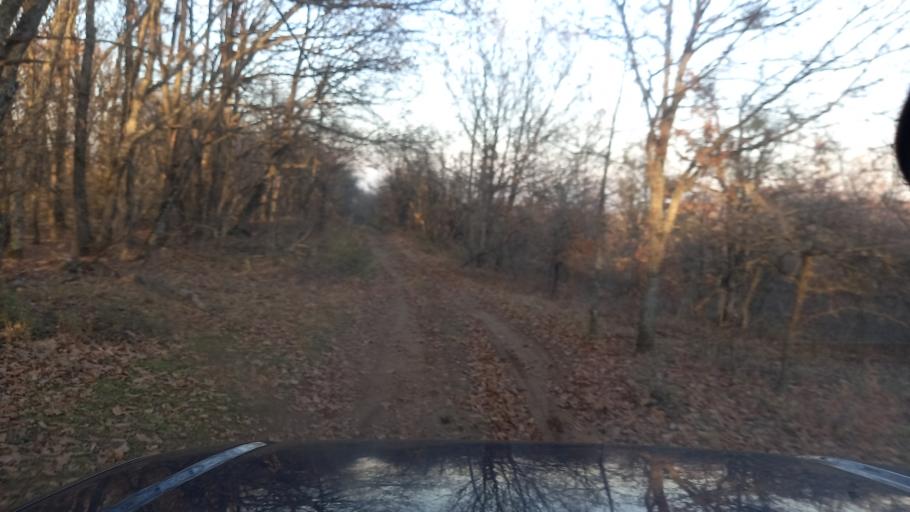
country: RU
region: Krasnodarskiy
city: Azovskaya
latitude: 44.8137
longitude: 38.6053
